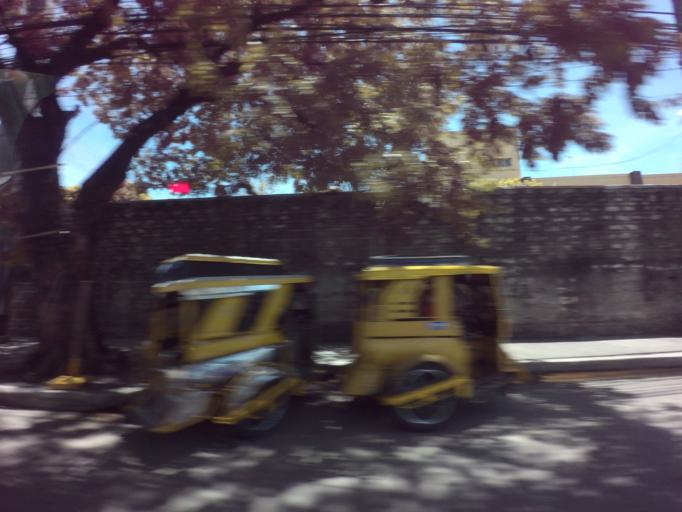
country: PH
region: Calabarzon
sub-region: Province of Rizal
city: Taguig
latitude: 14.4931
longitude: 121.0401
